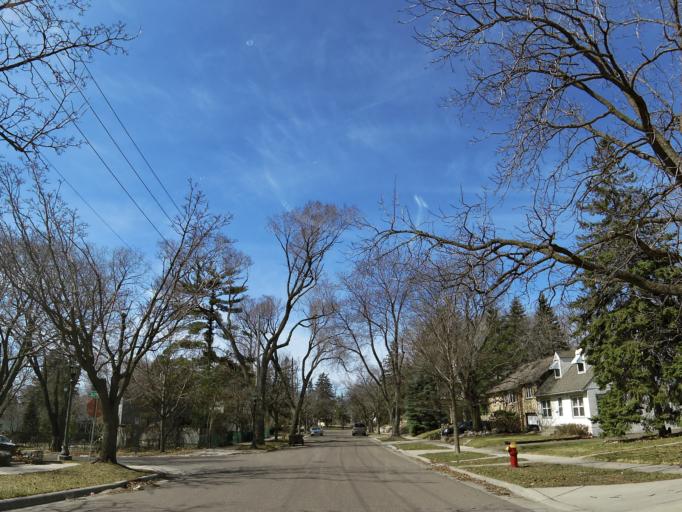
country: US
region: Minnesota
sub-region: Ramsey County
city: Saint Paul
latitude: 44.9487
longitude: -93.0584
